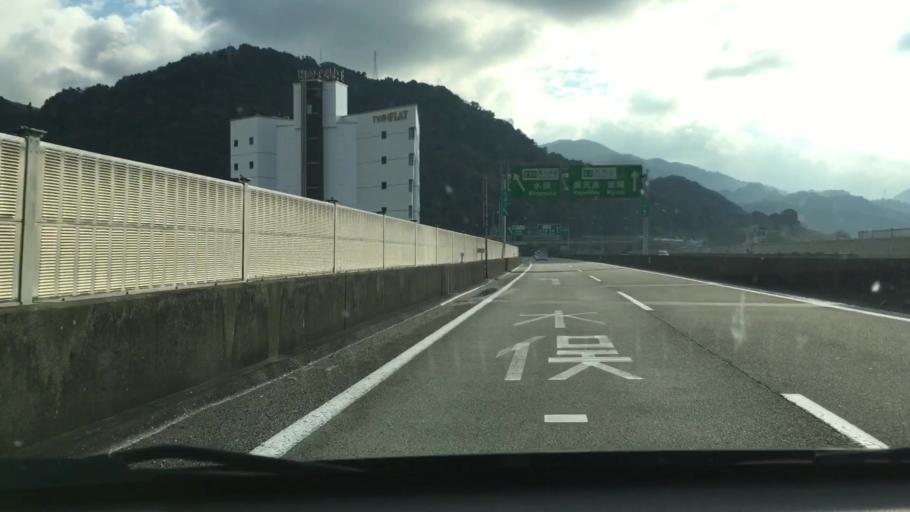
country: JP
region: Kumamoto
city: Yatsushiro
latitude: 32.5074
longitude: 130.6465
